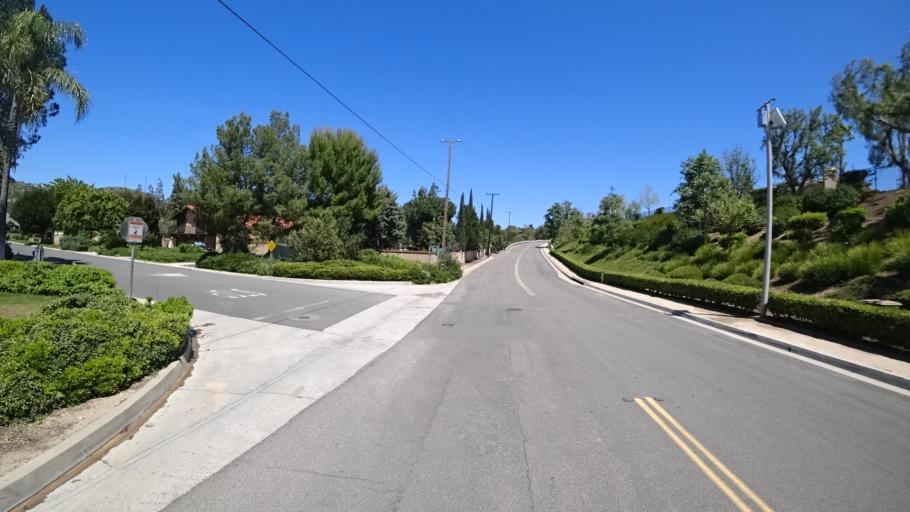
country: US
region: California
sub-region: Orange County
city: Villa Park
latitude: 33.8231
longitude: -117.8079
